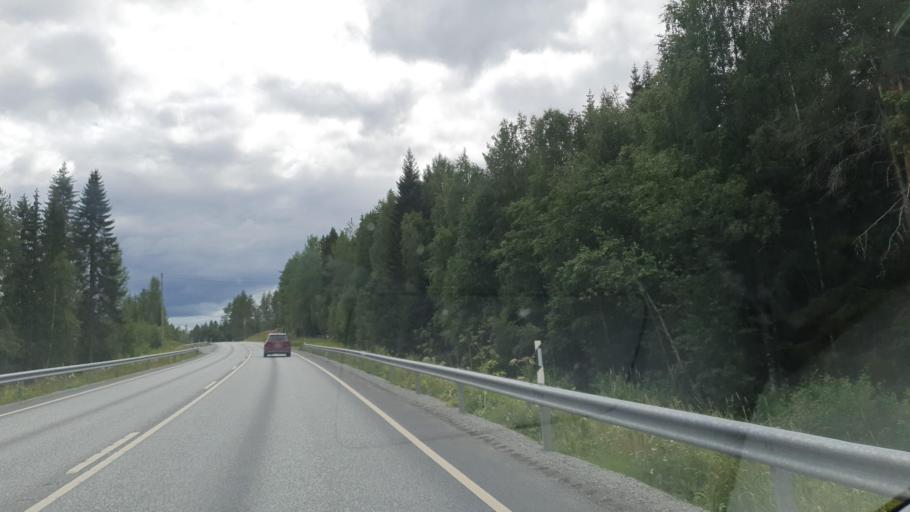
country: FI
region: Northern Savo
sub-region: Ylae-Savo
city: Sonkajaervi
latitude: 63.8354
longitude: 27.4225
